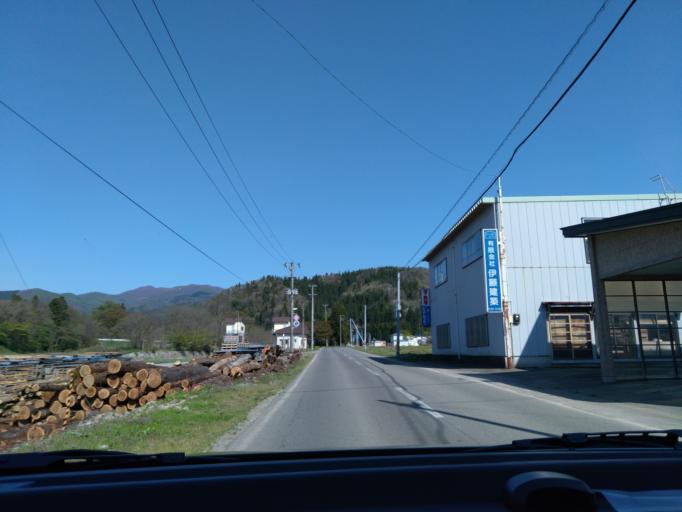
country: JP
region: Akita
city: Yokotemachi
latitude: 39.4160
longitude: 140.5855
